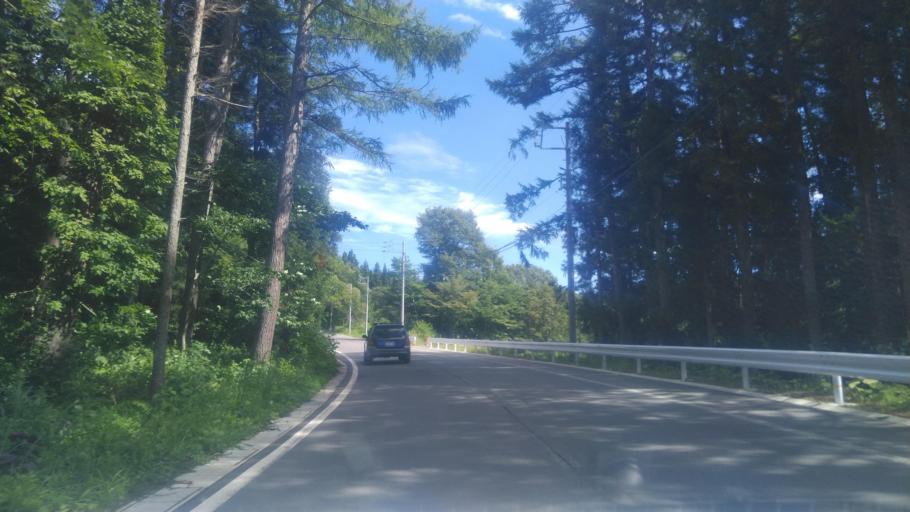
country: JP
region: Niigata
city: Arai
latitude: 36.8345
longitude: 138.1695
